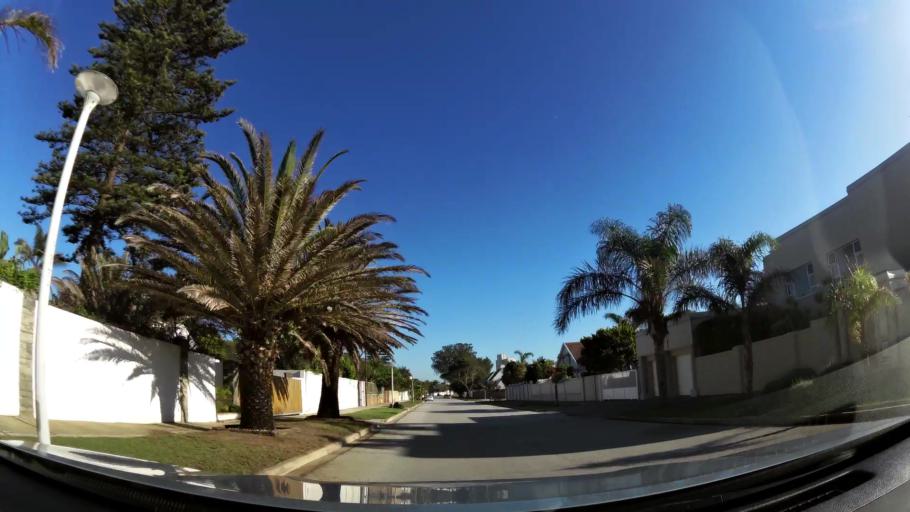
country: ZA
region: Eastern Cape
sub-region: Nelson Mandela Bay Metropolitan Municipality
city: Port Elizabeth
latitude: -33.9871
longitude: 25.6657
